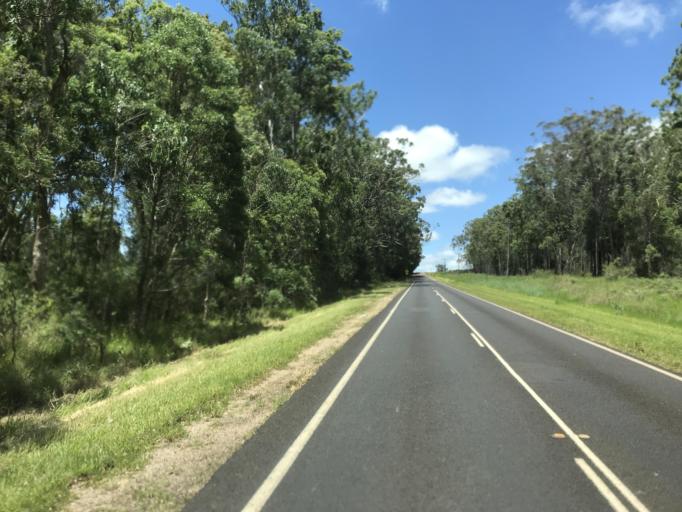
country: AU
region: Queensland
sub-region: Tablelands
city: Ravenshoe
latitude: -17.5346
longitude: 145.4524
